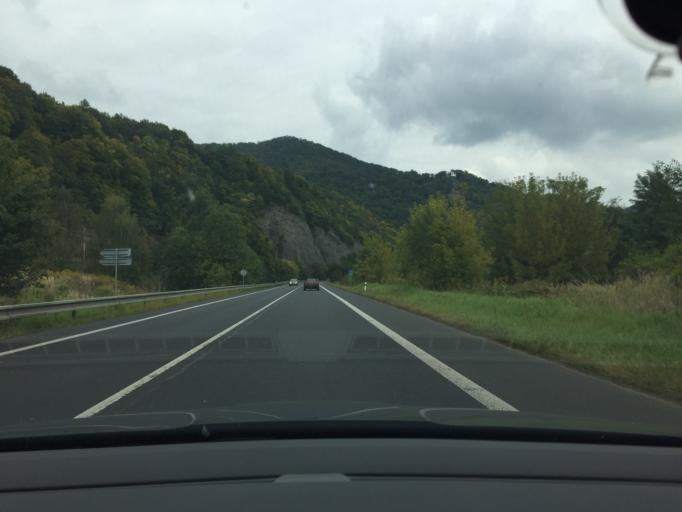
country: CZ
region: Ustecky
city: Povrly
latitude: 50.6767
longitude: 14.1658
